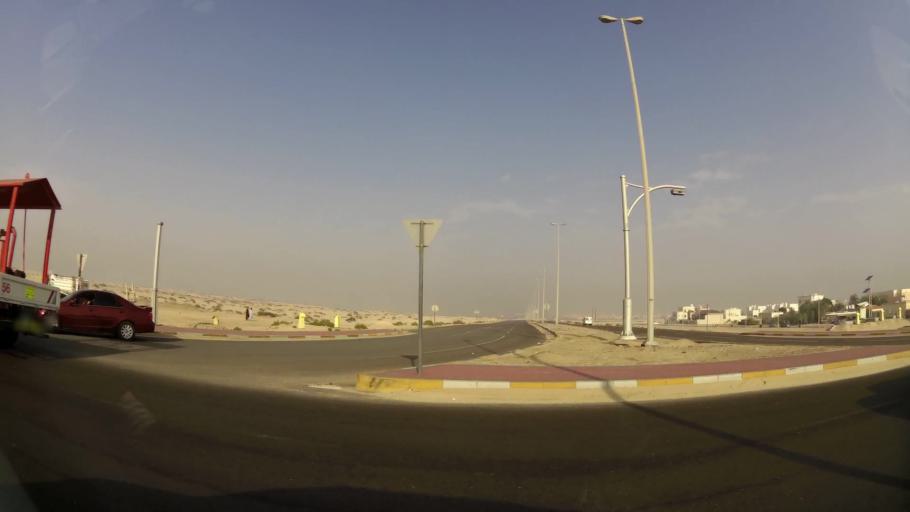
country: AE
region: Abu Dhabi
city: Abu Dhabi
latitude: 24.2755
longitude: 54.6423
